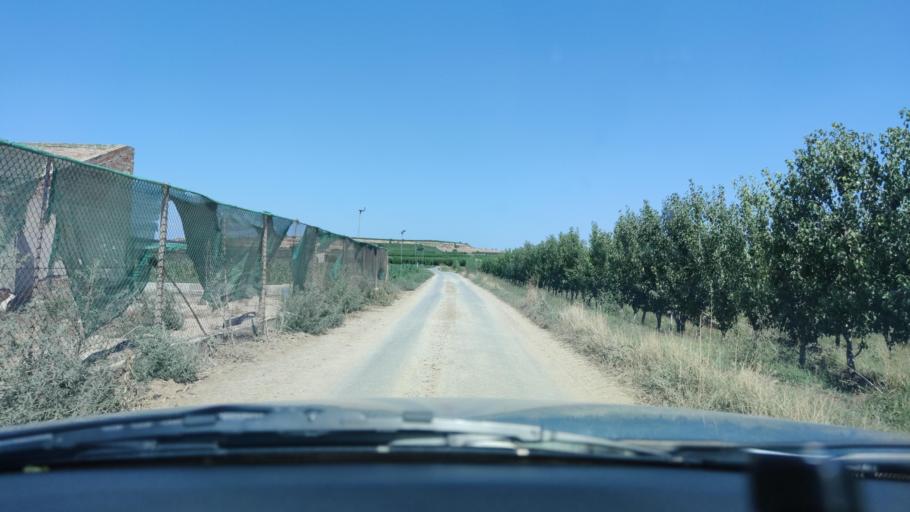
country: ES
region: Catalonia
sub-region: Provincia de Lleida
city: Corbins
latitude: 41.6766
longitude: 0.6580
